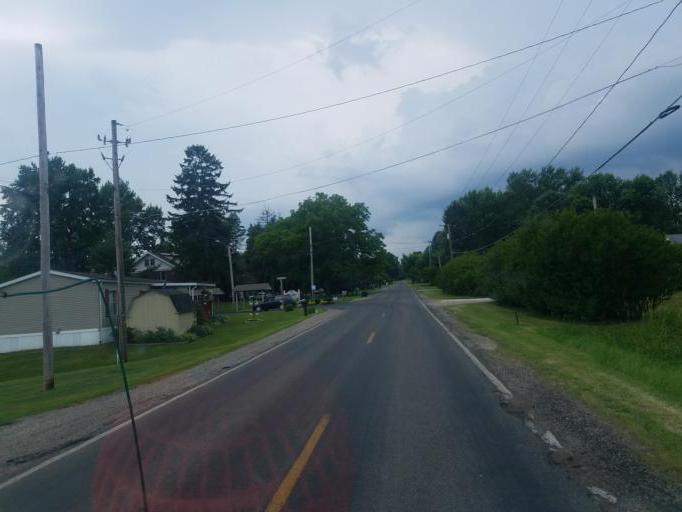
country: US
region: Ohio
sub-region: Stark County
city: Hartville
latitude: 41.0332
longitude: -81.2632
